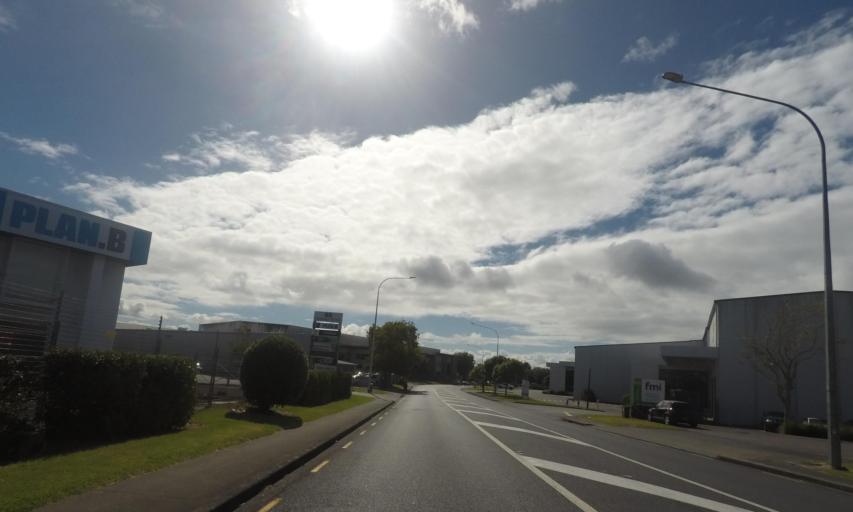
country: NZ
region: Auckland
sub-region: Auckland
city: Tamaki
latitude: -36.9202
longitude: 174.8485
